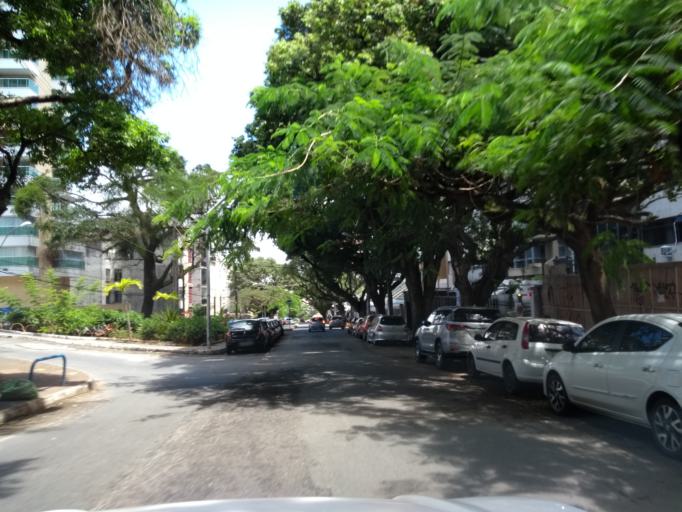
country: BR
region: Bahia
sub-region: Salvador
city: Salvador
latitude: -13.0008
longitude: -38.5242
